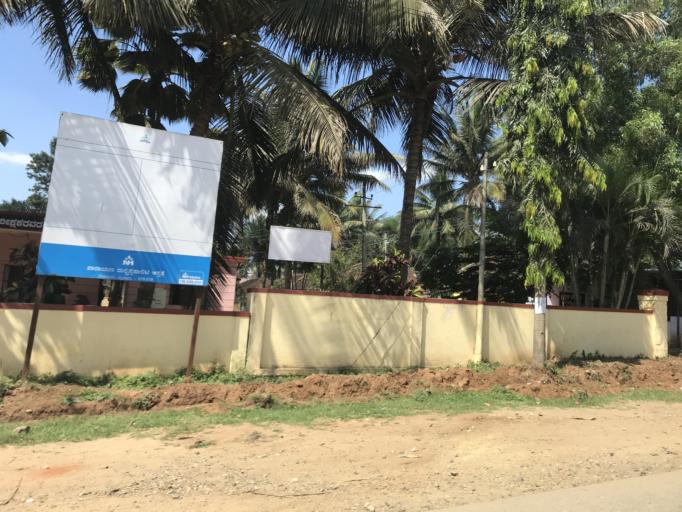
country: IN
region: Karnataka
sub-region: Mysore
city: Heggadadevankote
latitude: 12.0902
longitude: 76.3320
